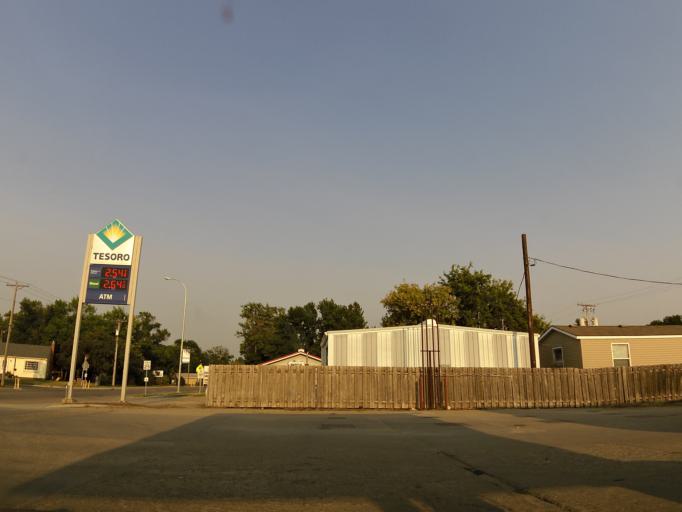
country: US
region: North Dakota
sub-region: Traill County
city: Mayville
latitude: 47.4979
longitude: -97.3221
